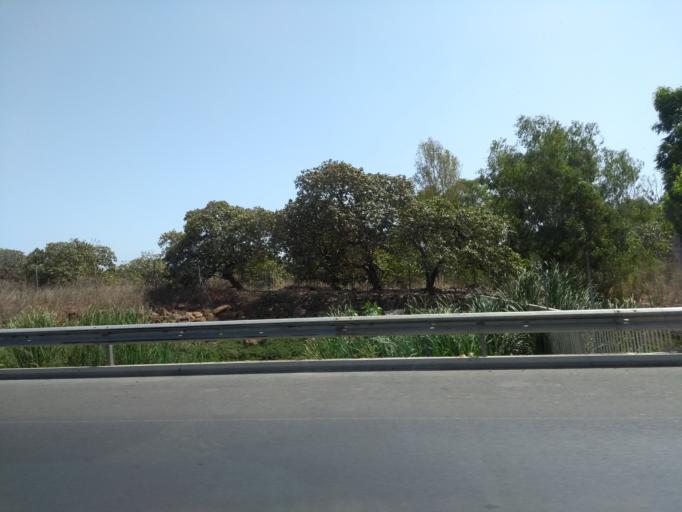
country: SN
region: Dakar
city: Pikine
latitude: 14.7545
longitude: -17.3138
